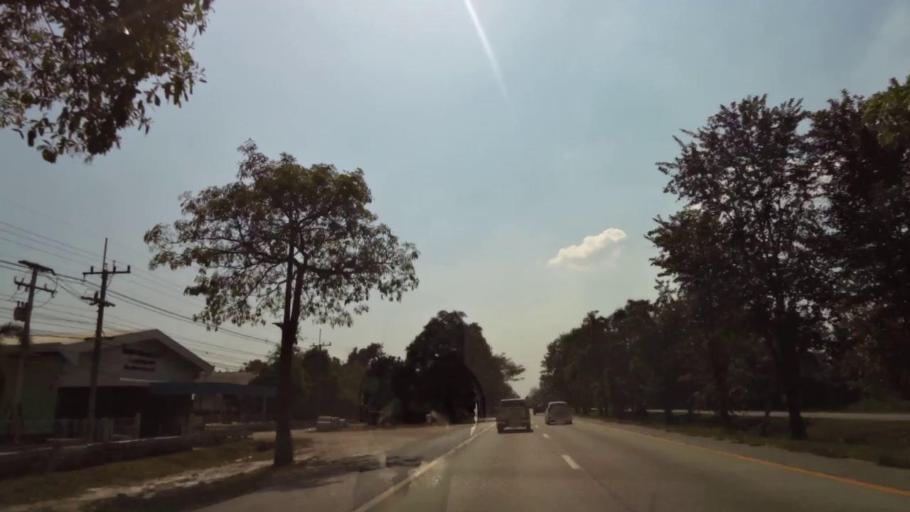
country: TH
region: Phichit
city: Wachira Barami
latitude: 16.5578
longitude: 100.1478
